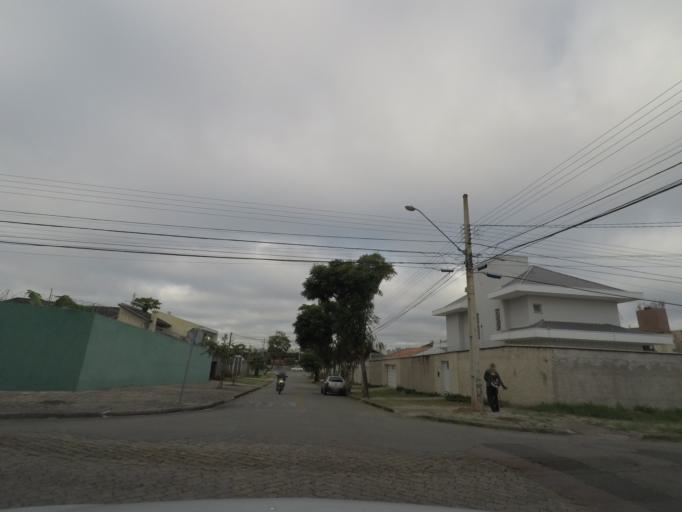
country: BR
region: Parana
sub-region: Curitiba
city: Curitiba
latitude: -25.4410
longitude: -49.2505
